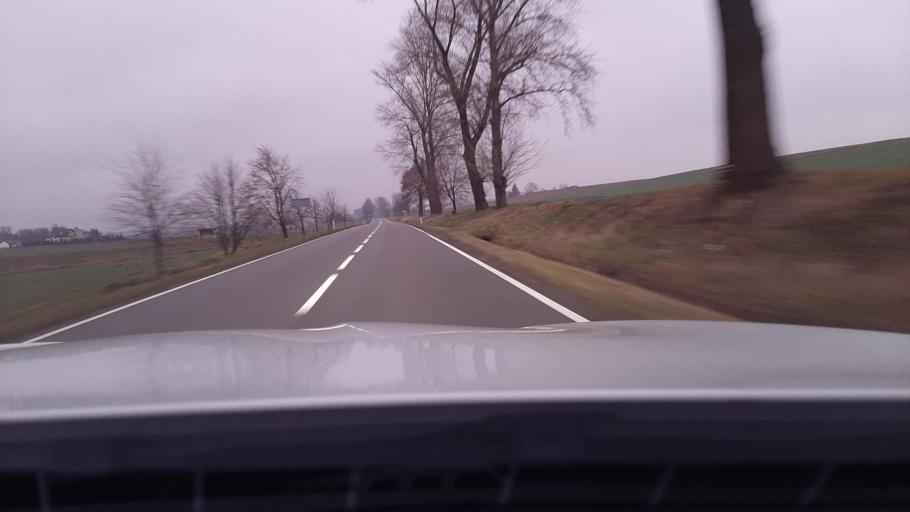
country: PL
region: Lublin Voivodeship
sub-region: Powiat lubelski
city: Garbow
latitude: 51.3470
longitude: 22.3774
